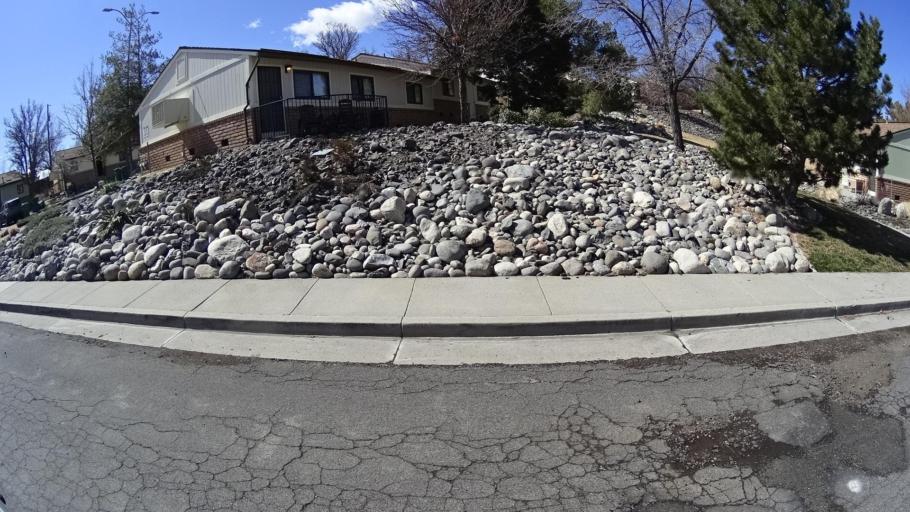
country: US
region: Nevada
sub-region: Washoe County
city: Golden Valley
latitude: 39.5928
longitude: -119.8438
